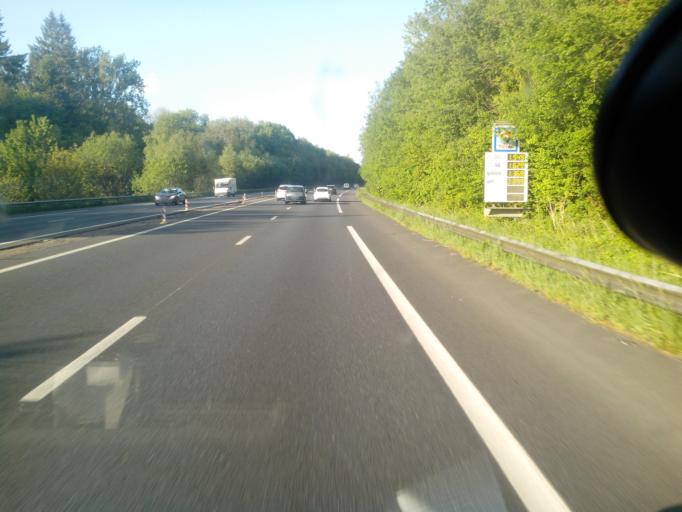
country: FR
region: Haute-Normandie
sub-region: Departement de la Seine-Maritime
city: Saint-Saens
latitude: 49.6716
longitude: 1.3191
